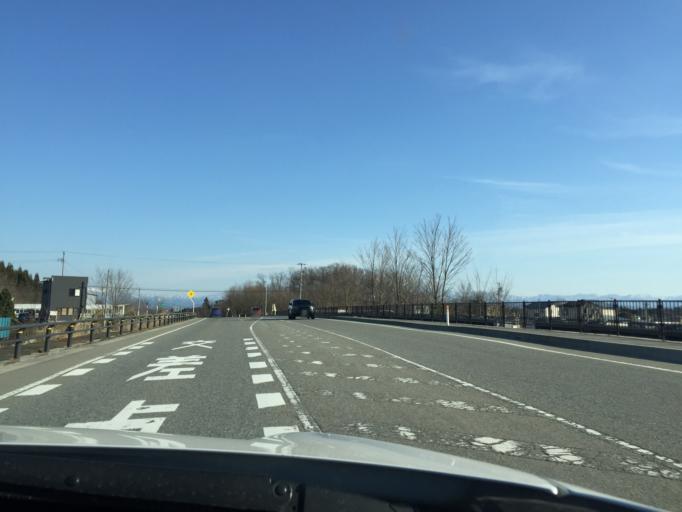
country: JP
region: Yamagata
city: Nagai
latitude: 38.0612
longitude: 140.0537
